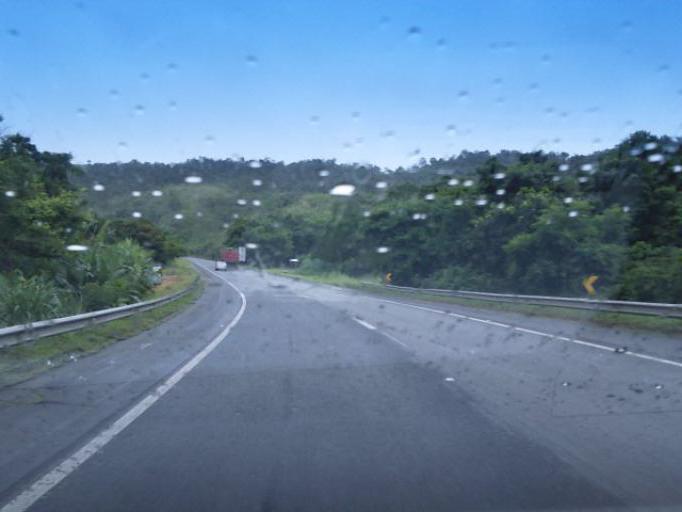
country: BR
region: Sao Paulo
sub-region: Cajati
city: Cajati
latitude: -24.7896
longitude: -48.2045
